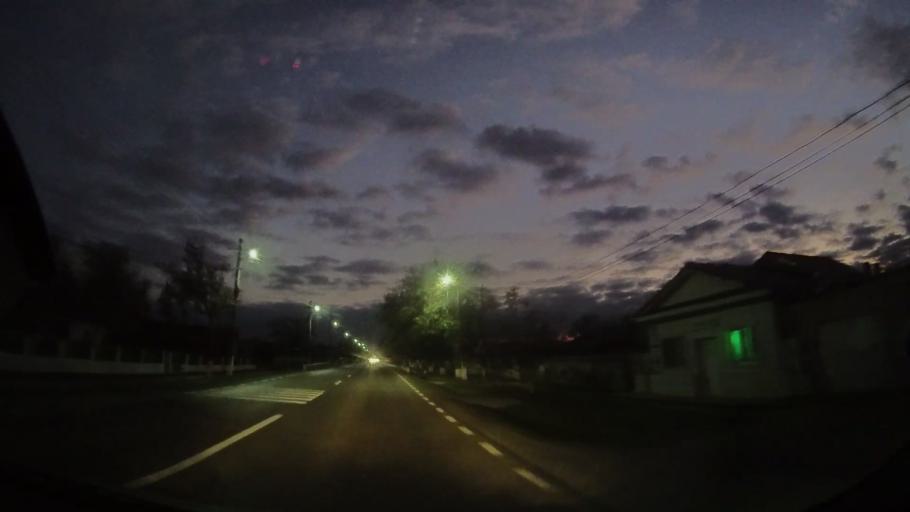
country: RO
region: Tulcea
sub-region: Comuna Mihail Kogalniceanu
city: Mihail Kogalniceanu
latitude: 45.0393
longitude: 28.7345
